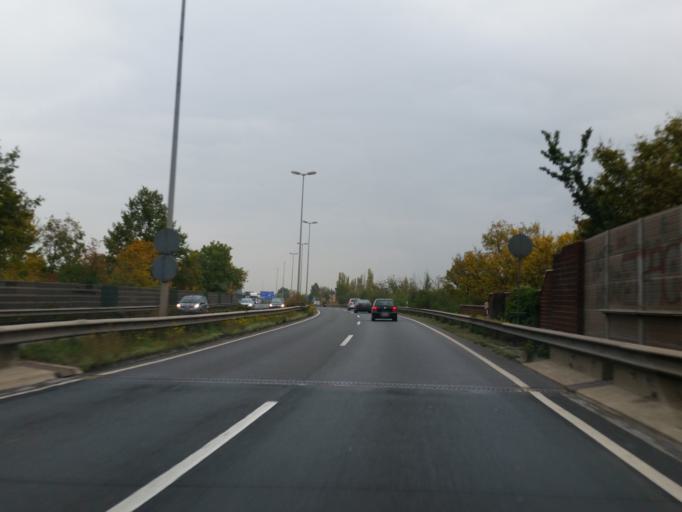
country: DE
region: Lower Saxony
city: Braunschweig
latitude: 52.2725
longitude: 10.4928
